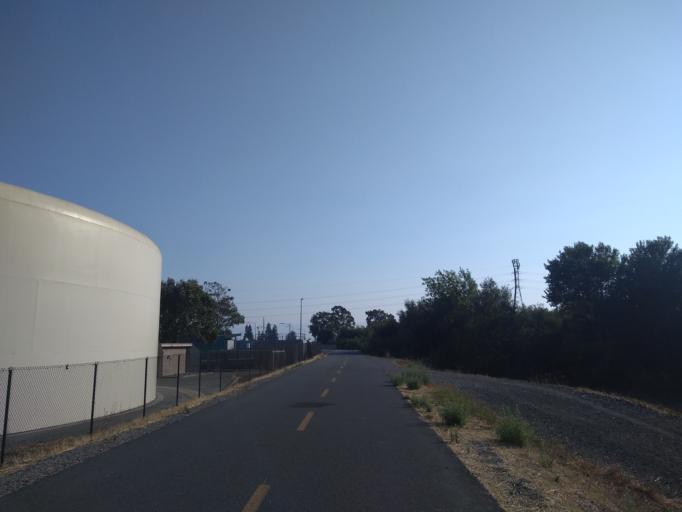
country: US
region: California
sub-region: Santa Clara County
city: Santa Clara
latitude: 37.3825
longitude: -121.9366
